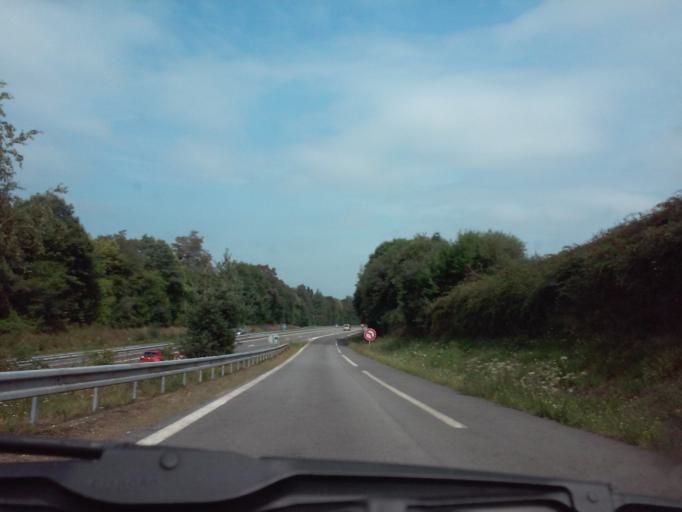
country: FR
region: Brittany
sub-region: Departement du Morbihan
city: Ploermel
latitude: 47.8856
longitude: -2.4152
